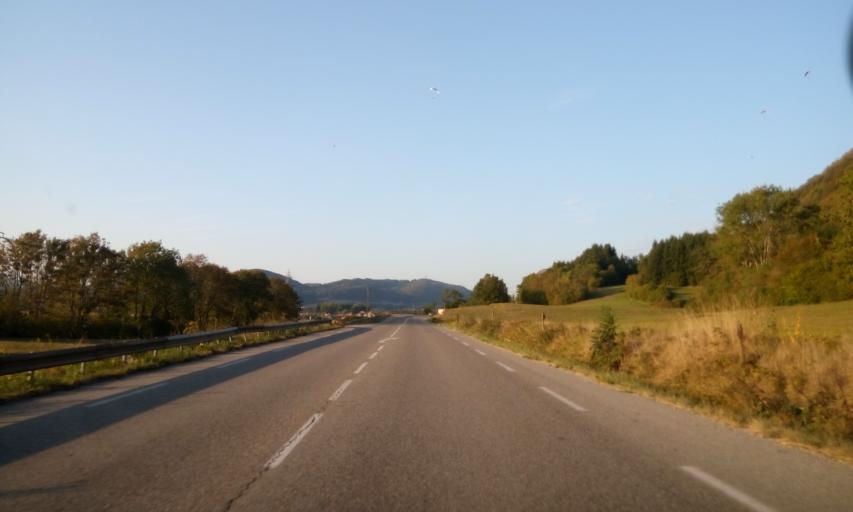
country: FR
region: Rhone-Alpes
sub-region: Departement de l'Ain
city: Saint-Martin-du-Frene
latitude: 46.1519
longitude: 5.5630
